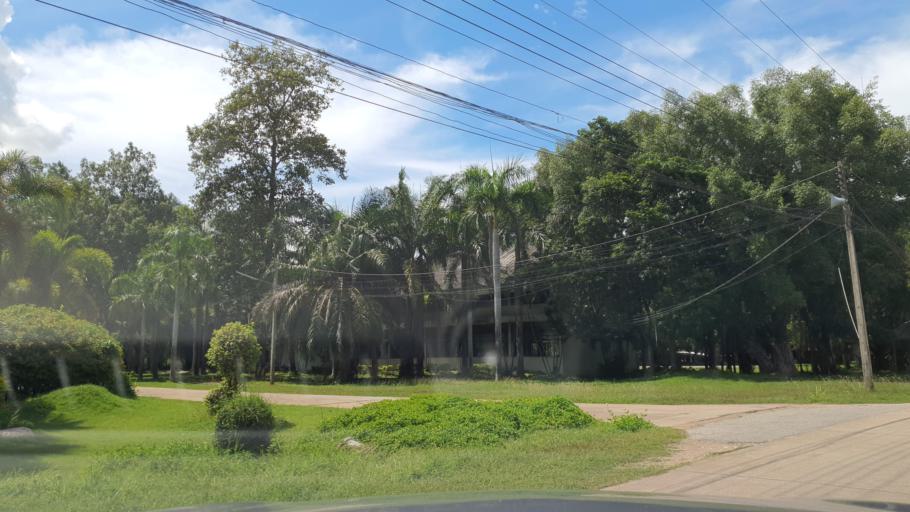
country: TH
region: Chiang Mai
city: San Pa Tong
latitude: 18.5801
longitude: 98.8742
